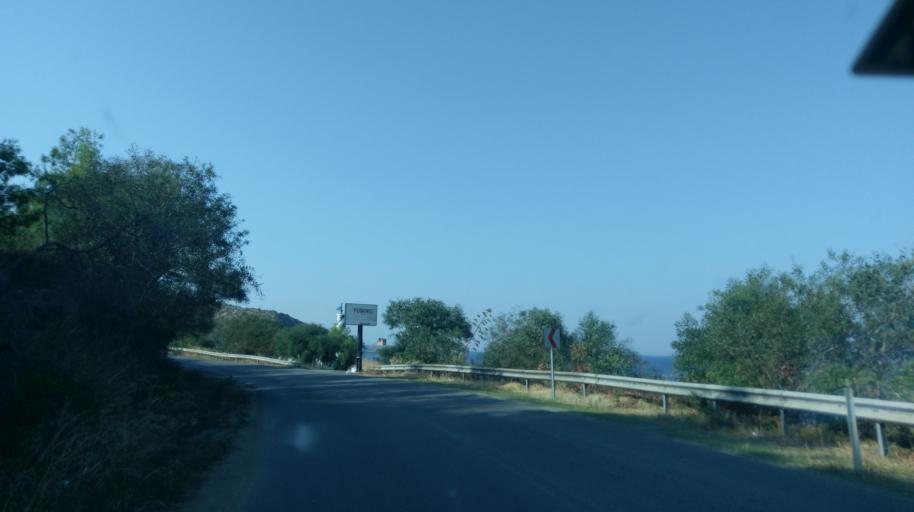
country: CY
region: Lefkosia
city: Lefka
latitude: 35.1534
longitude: 32.7922
